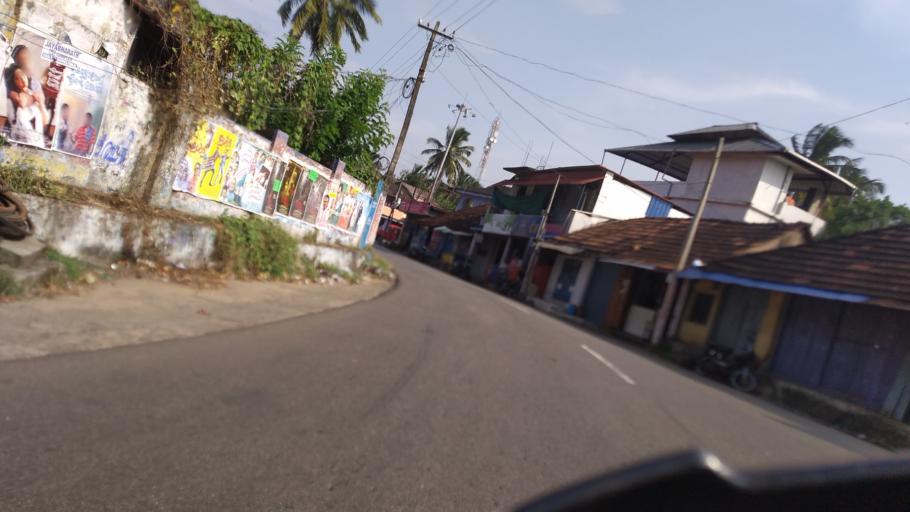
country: IN
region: Kerala
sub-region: Palakkad district
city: Palakkad
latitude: 10.5996
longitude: 76.5507
